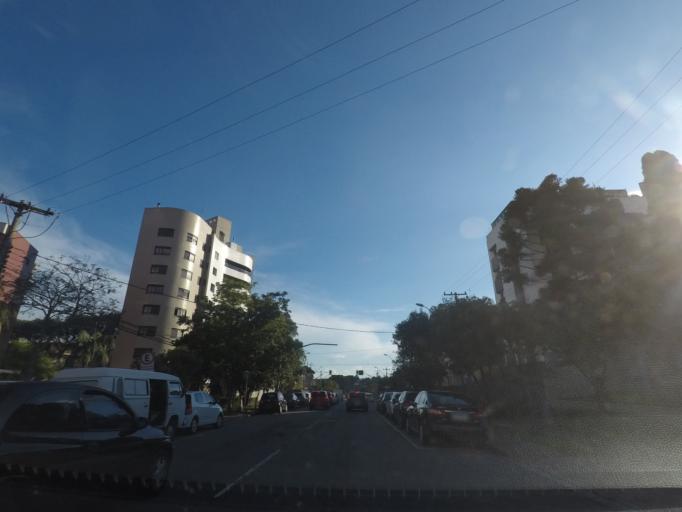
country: BR
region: Parana
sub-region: Curitiba
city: Curitiba
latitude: -25.4499
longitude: -49.2988
